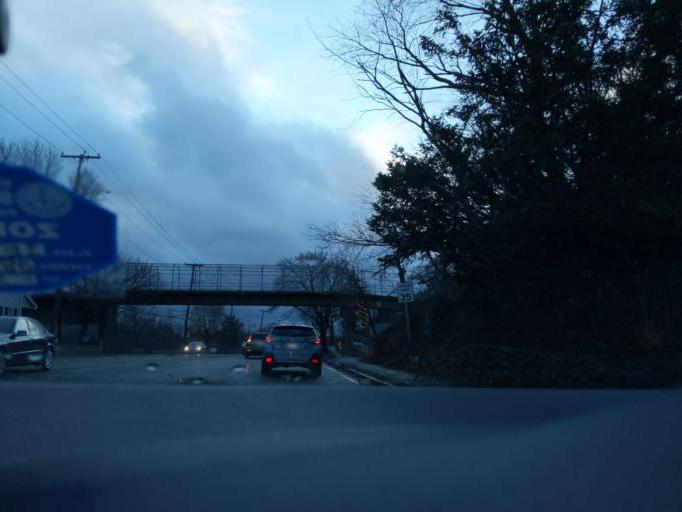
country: US
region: Massachusetts
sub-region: Essex County
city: Salem
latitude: 42.5084
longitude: -70.9125
